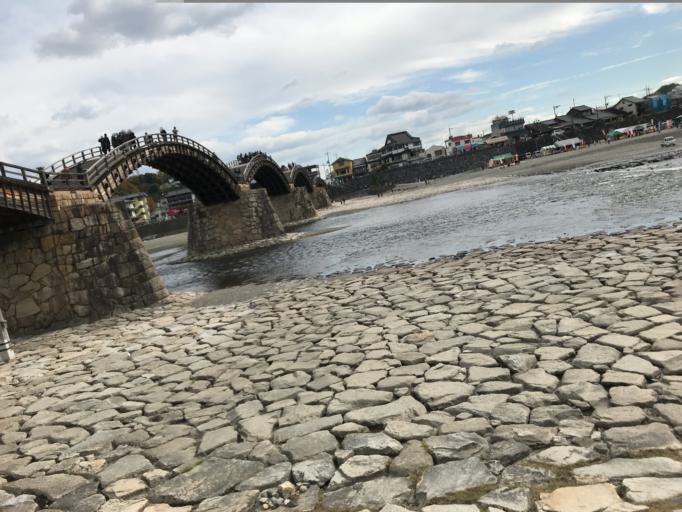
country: JP
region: Yamaguchi
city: Iwakuni
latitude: 34.1680
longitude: 132.1774
